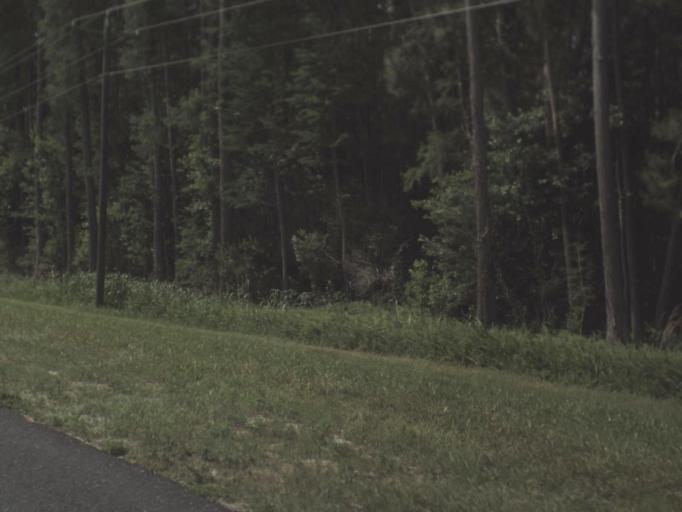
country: US
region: Florida
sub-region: Alachua County
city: Waldo
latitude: 29.7722
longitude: -82.1555
